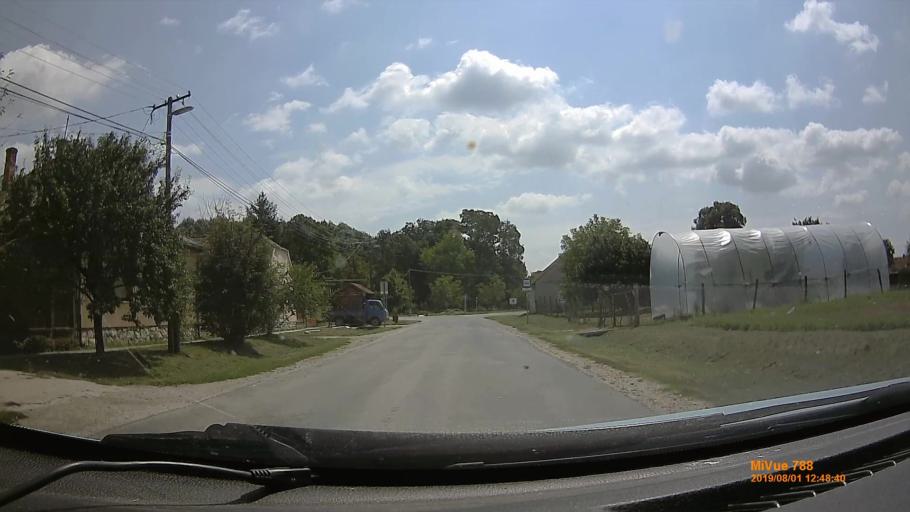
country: HR
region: Osjecko-Baranjska
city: Viljevo
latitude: 45.8174
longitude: 18.1073
